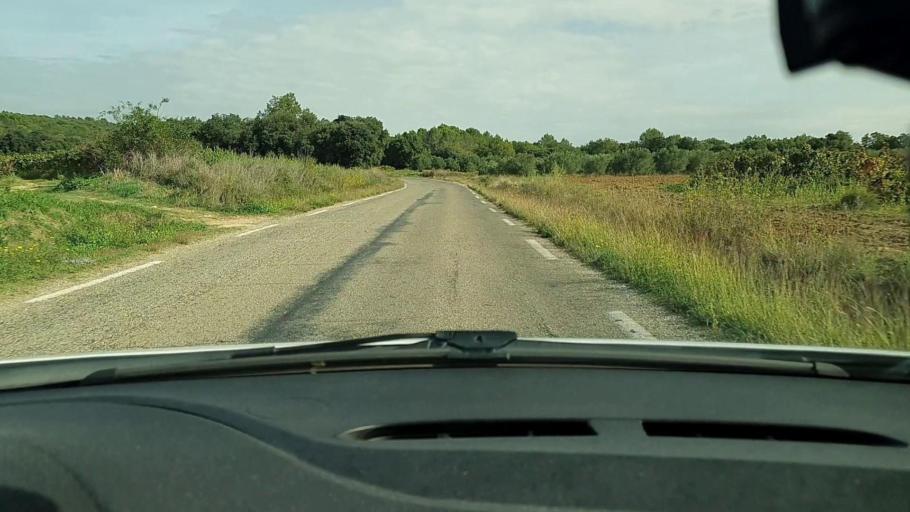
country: FR
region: Languedoc-Roussillon
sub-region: Departement du Gard
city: Saint-Quentin-la-Poterie
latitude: 44.0633
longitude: 4.4406
